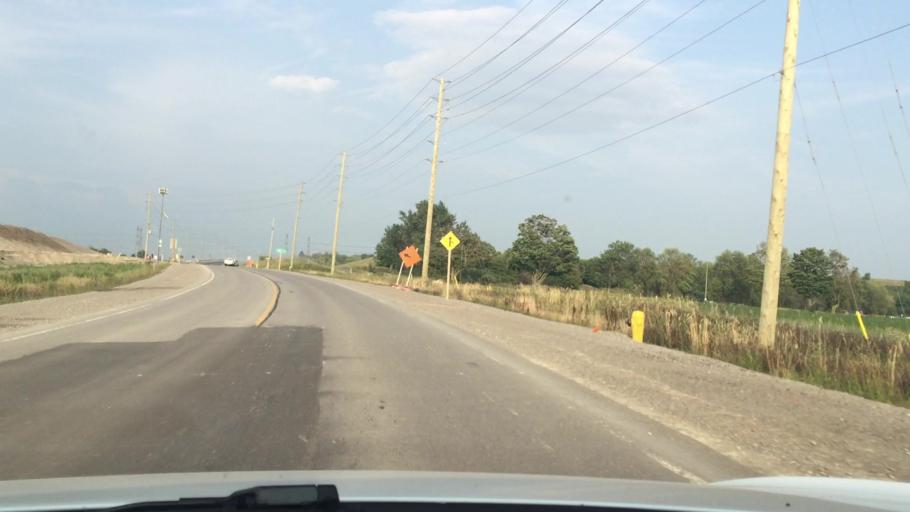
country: CA
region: Ontario
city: Oshawa
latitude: 43.8795
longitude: -78.7450
